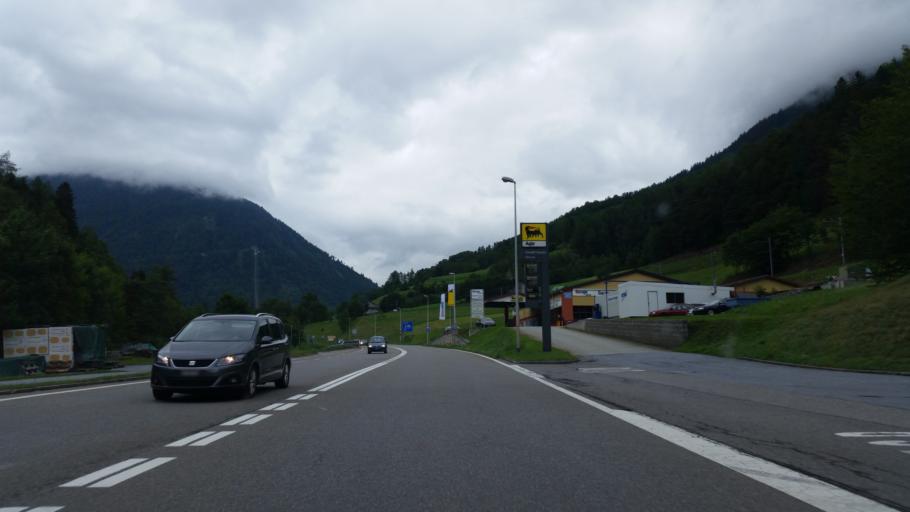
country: CH
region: Valais
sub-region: Entremont District
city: Orsieres
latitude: 46.0423
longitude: 7.1480
